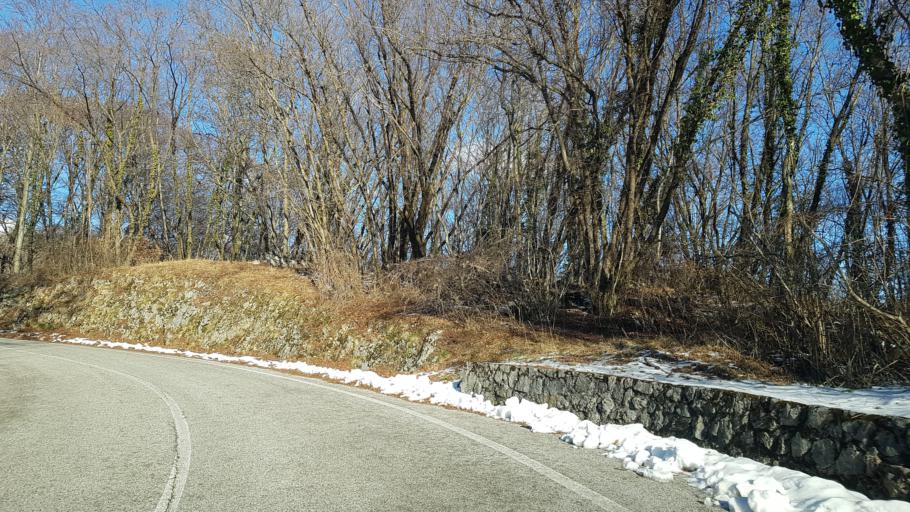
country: IT
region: Friuli Venezia Giulia
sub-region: Provincia di Udine
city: Forgaria nel Friuli
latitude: 46.2384
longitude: 12.9908
